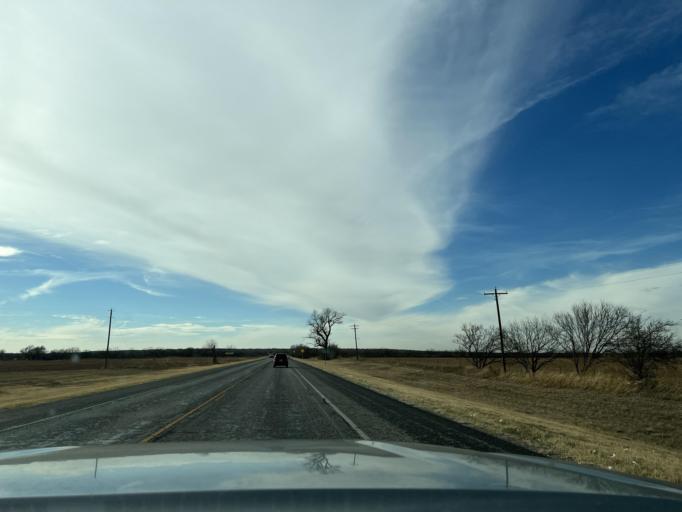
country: US
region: Texas
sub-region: Fisher County
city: Roby
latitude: 32.7612
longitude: -100.3024
